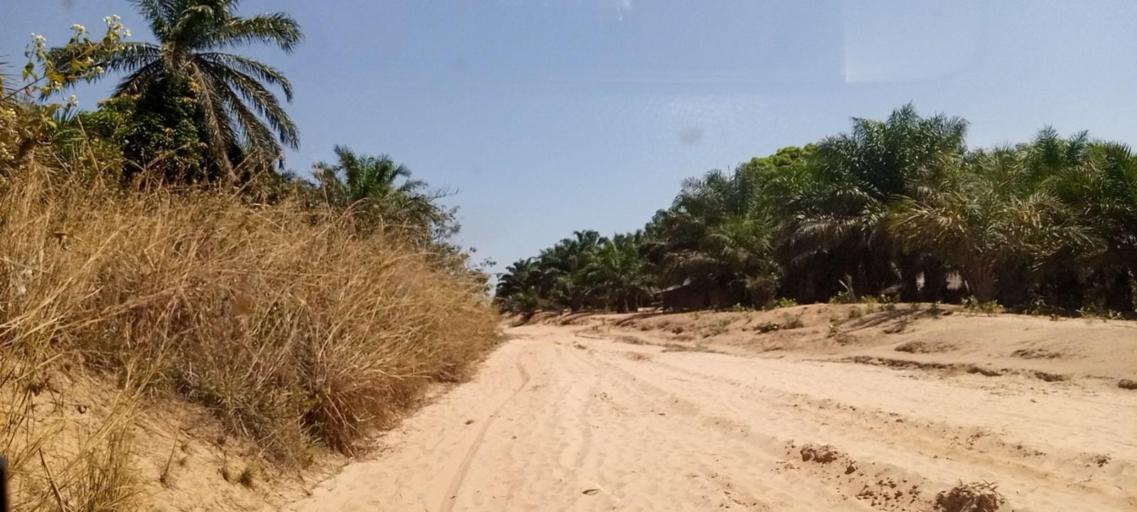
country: CD
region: Kasai-Oriental
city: Kabinda
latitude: -5.9597
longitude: 24.7884
